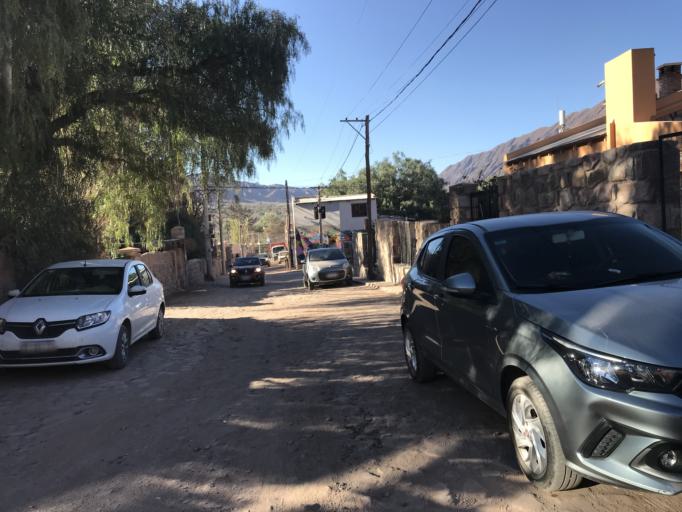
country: AR
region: Jujuy
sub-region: Departamento de Tilcara
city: Tilcara
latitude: -23.5779
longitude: -65.3960
